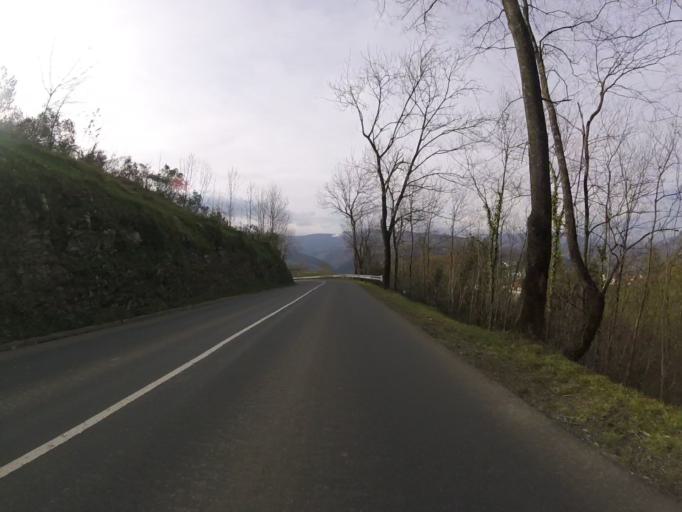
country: ES
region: Basque Country
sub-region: Provincia de Guipuzcoa
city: Beizama
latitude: 43.1672
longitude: -2.2268
